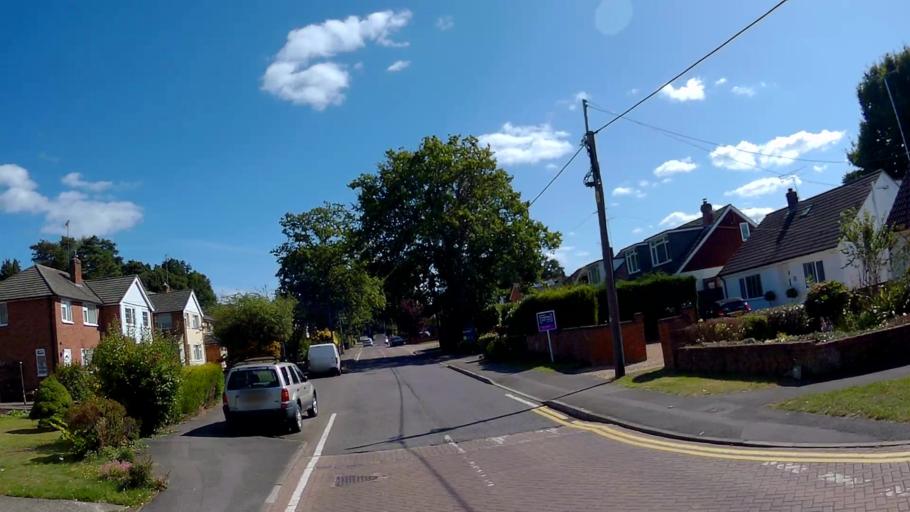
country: GB
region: England
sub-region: Bracknell Forest
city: Crowthorne
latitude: 51.3799
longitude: -0.7943
